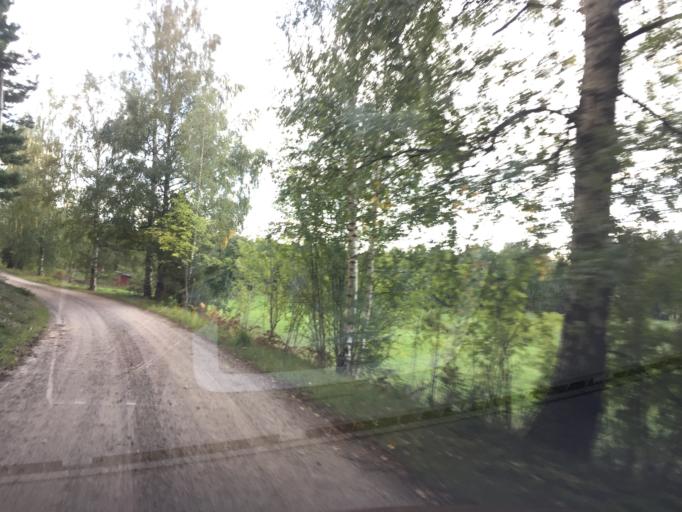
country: SE
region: Soedermanland
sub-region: Vingakers Kommun
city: Vingaker
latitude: 58.9900
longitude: 15.7326
